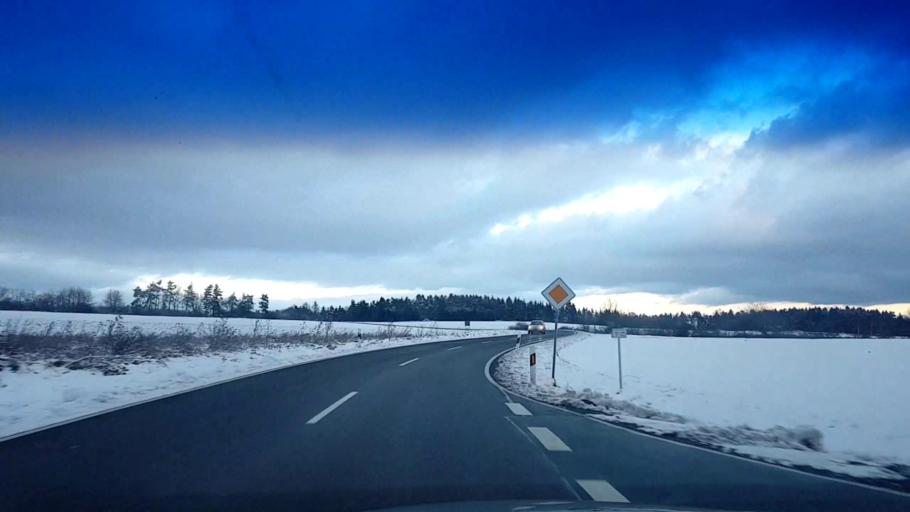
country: DE
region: Bavaria
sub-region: Upper Franconia
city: Buttenheim
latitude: 49.8594
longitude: 11.0893
